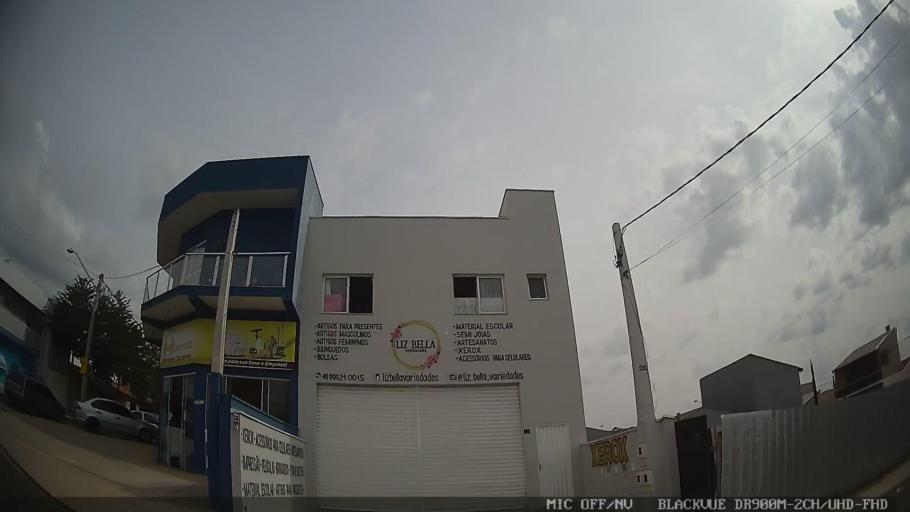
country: BR
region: Sao Paulo
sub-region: Indaiatuba
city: Indaiatuba
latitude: -23.0980
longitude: -47.2750
